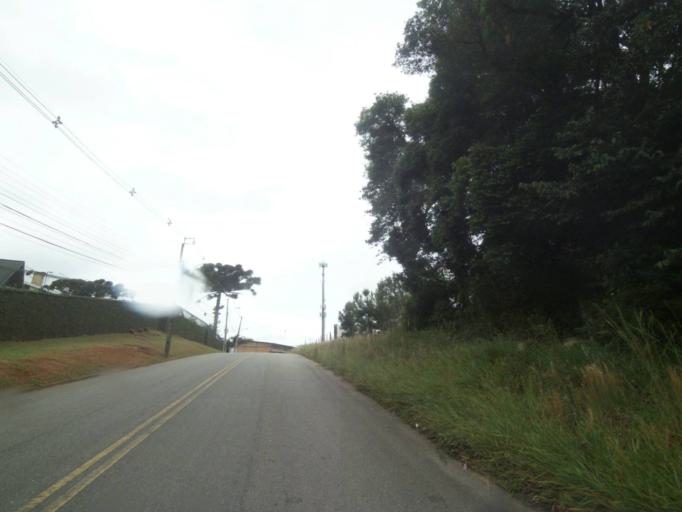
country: BR
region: Parana
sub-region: Curitiba
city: Curitiba
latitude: -25.4566
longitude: -49.3359
